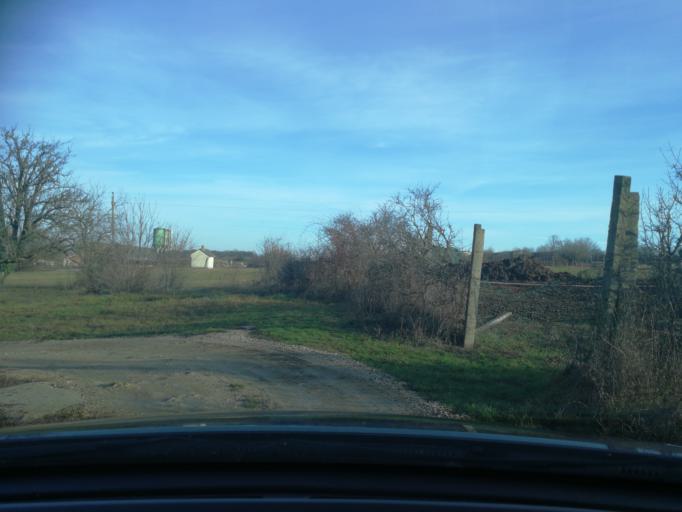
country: HU
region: Veszprem
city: Nemesvamos
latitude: 47.0111
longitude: 17.7932
